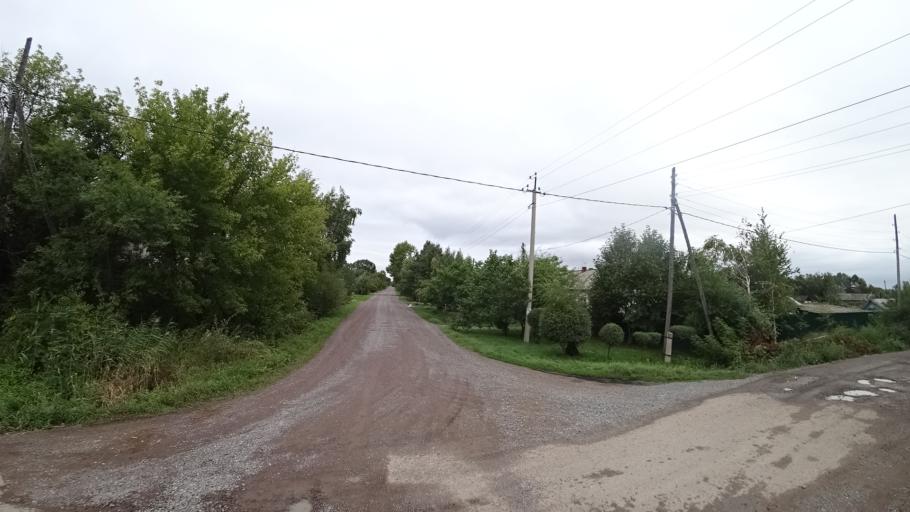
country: RU
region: Primorskiy
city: Chernigovka
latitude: 44.3362
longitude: 132.5944
